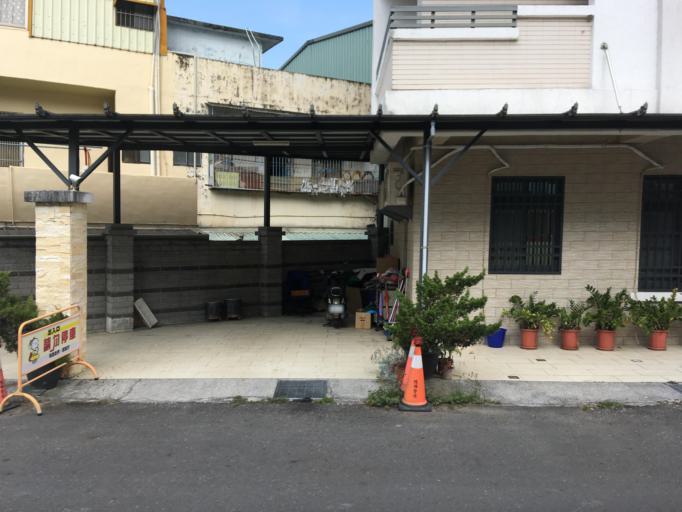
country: TW
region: Taiwan
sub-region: Chiayi
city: Jiayi Shi
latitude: 23.4912
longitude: 120.5042
